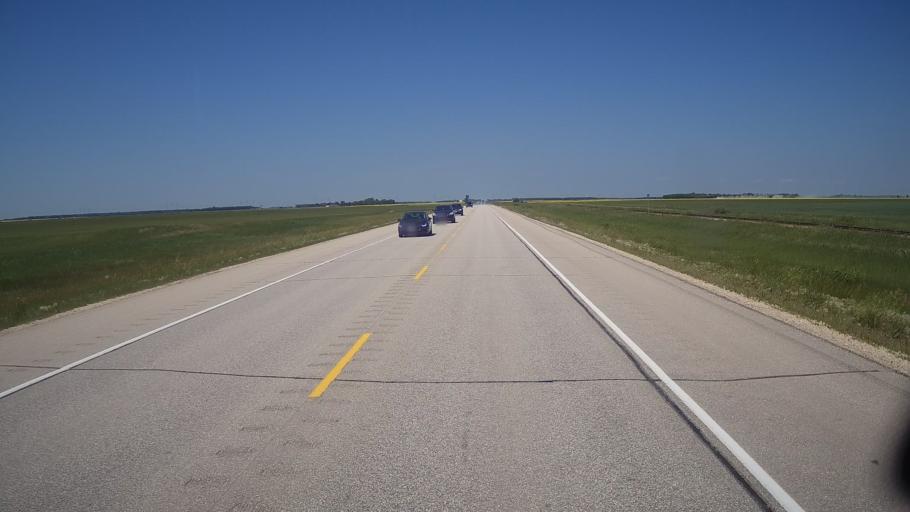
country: CA
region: Manitoba
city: Stonewall
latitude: 50.0216
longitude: -97.3770
